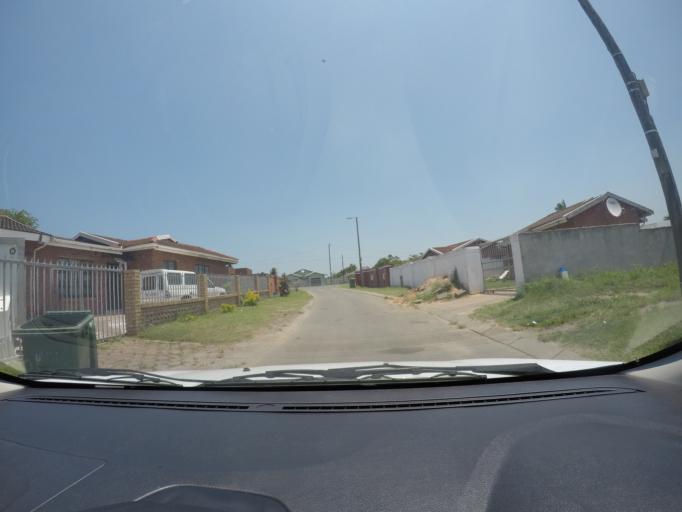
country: ZA
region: KwaZulu-Natal
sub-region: uThungulu District Municipality
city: eSikhawini
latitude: -28.8883
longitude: 31.8933
